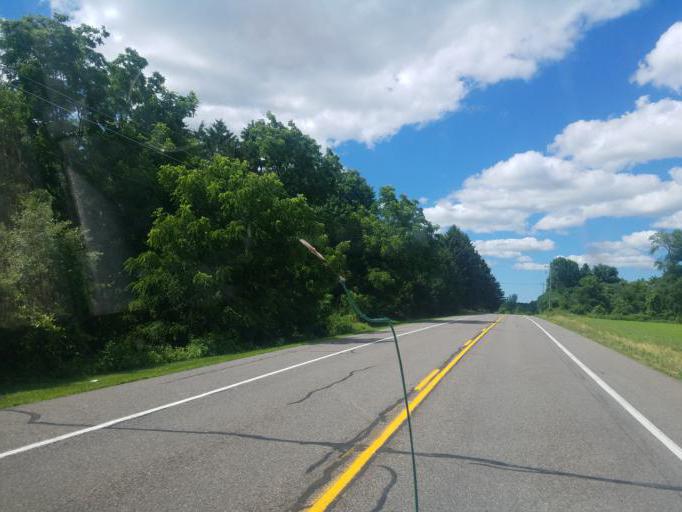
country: US
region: New York
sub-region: Ontario County
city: Phelps
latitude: 42.9815
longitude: -76.9780
